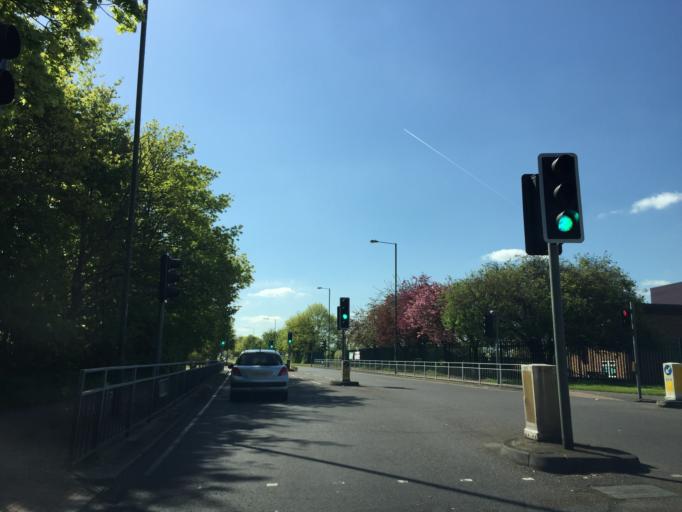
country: GB
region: England
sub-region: Essex
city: Harlow
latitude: 51.7584
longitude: 0.0891
